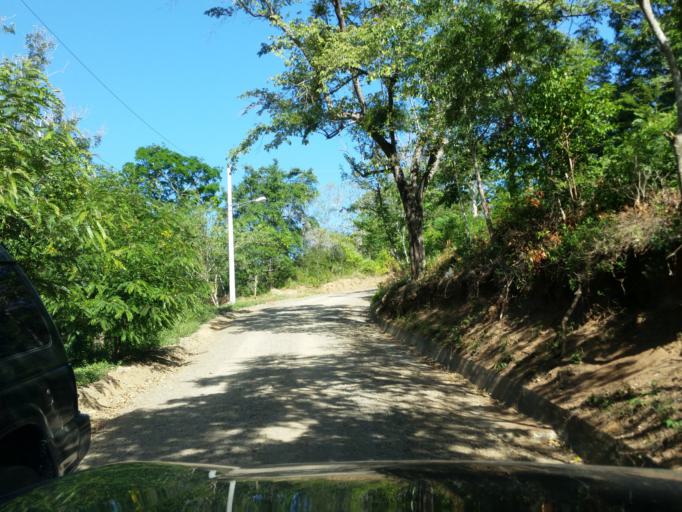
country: NI
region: Rivas
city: San Juan del Sur
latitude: 11.2725
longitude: -85.8432
